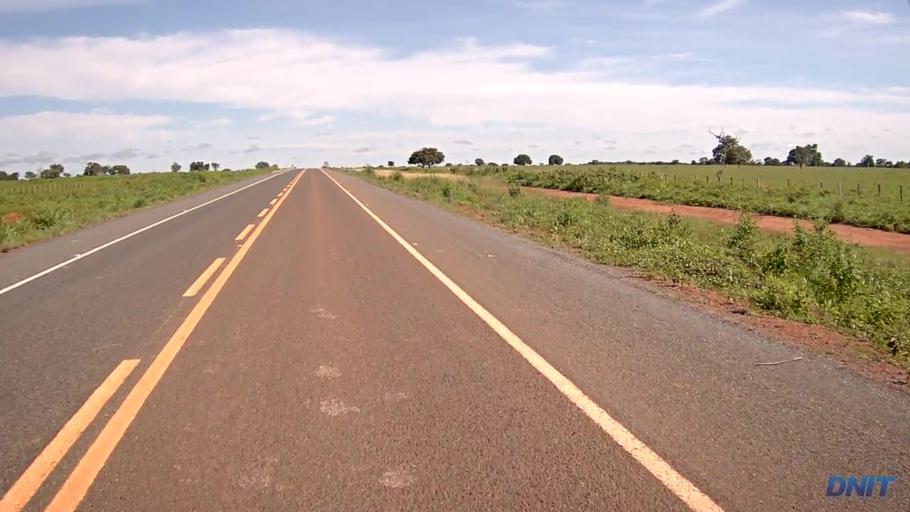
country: BR
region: Goias
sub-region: Sao Miguel Do Araguaia
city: Sao Miguel do Araguaia
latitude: -13.4892
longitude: -50.1095
